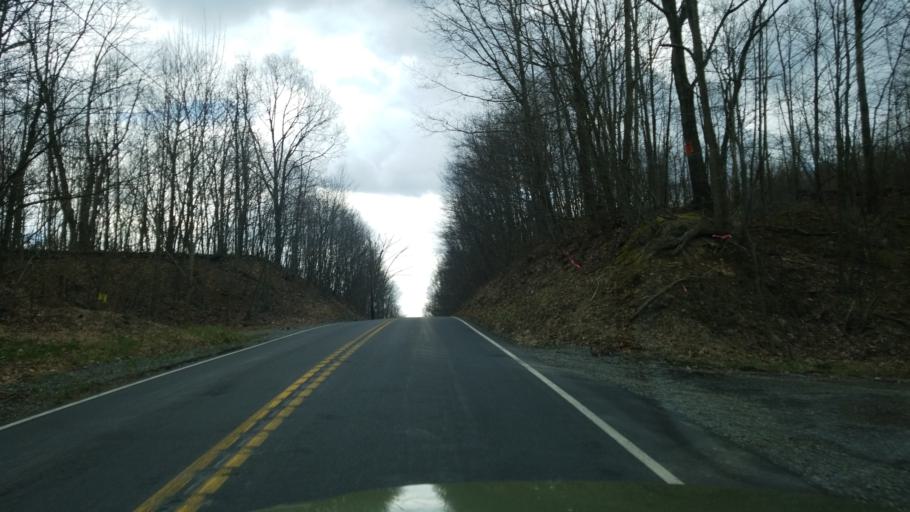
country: US
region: Pennsylvania
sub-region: Clearfield County
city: Curwensville
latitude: 40.8751
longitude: -78.4563
